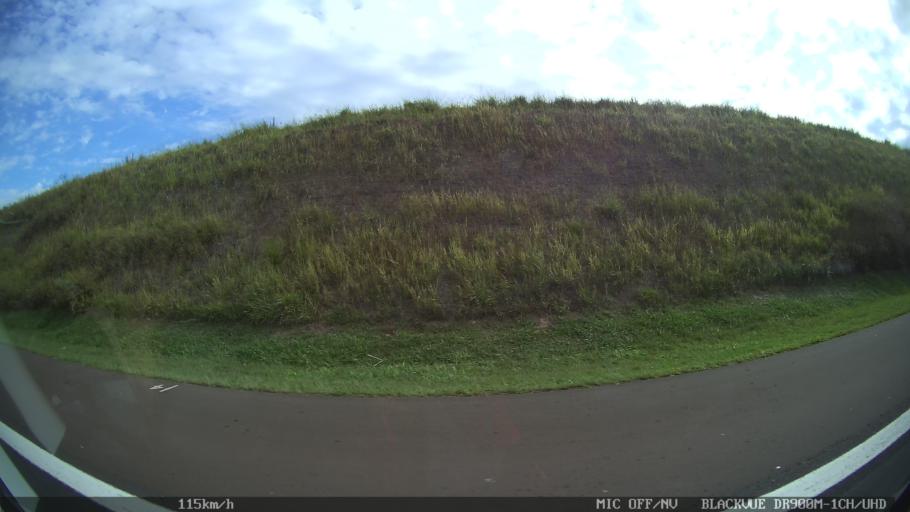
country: BR
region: Sao Paulo
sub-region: Iracemapolis
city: Iracemapolis
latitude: -22.6184
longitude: -47.4610
